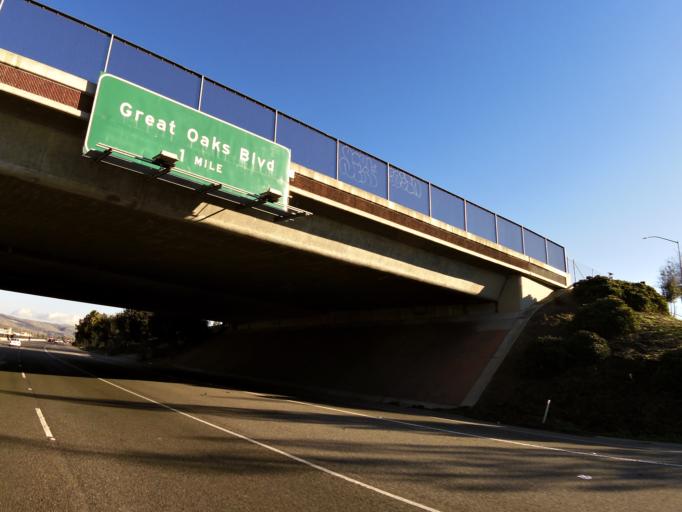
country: US
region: California
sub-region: Santa Clara County
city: Seven Trees
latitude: 37.2428
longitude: -121.8044
